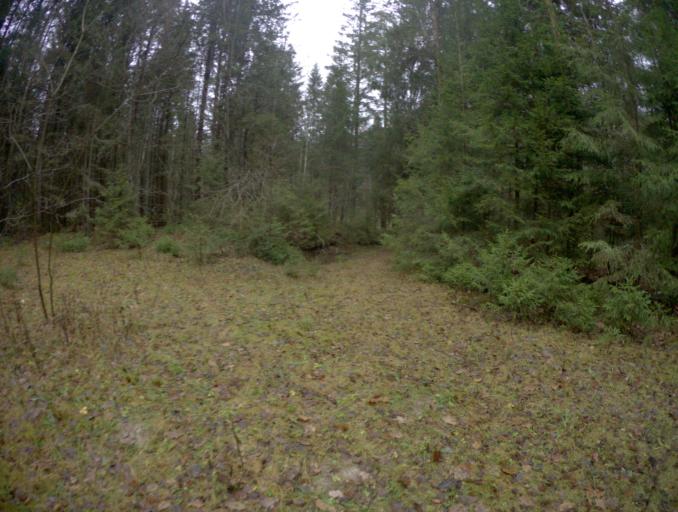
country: RU
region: Vladimir
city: Golovino
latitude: 56.0161
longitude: 40.5071
